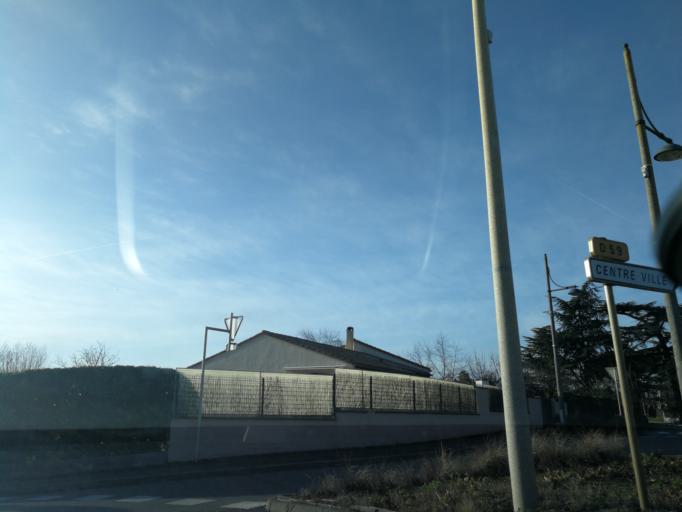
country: FR
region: Midi-Pyrenees
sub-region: Departement de la Haute-Garonne
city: Saint-Jean
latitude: 43.6527
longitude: 1.4943
